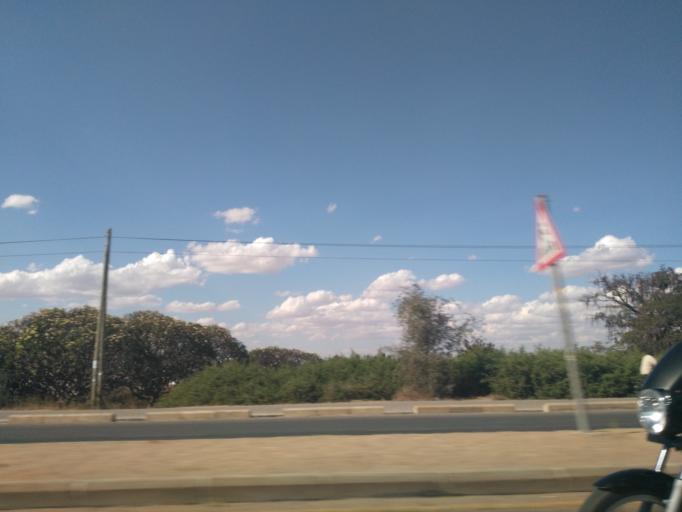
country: TZ
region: Dodoma
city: Dodoma
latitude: -6.1723
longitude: 35.7326
